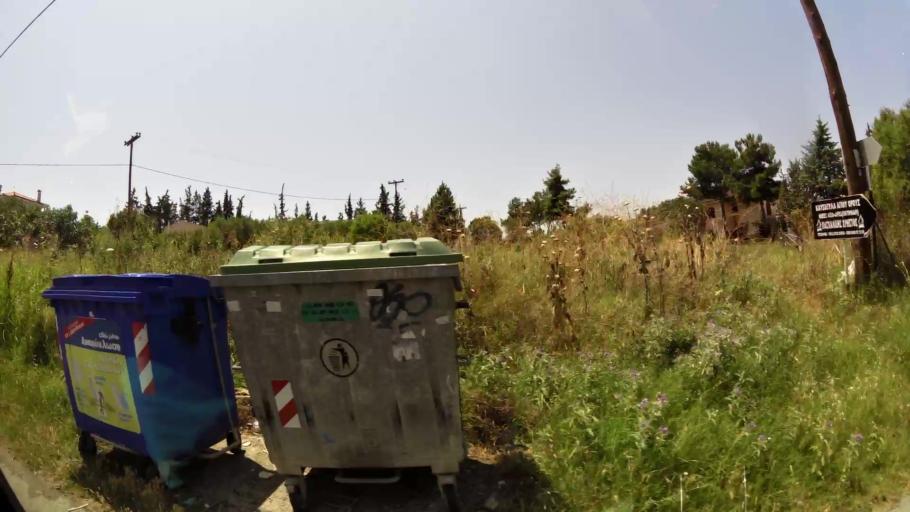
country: GR
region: Central Macedonia
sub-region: Nomos Thessalonikis
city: Trilofos
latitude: 40.4702
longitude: 22.9744
